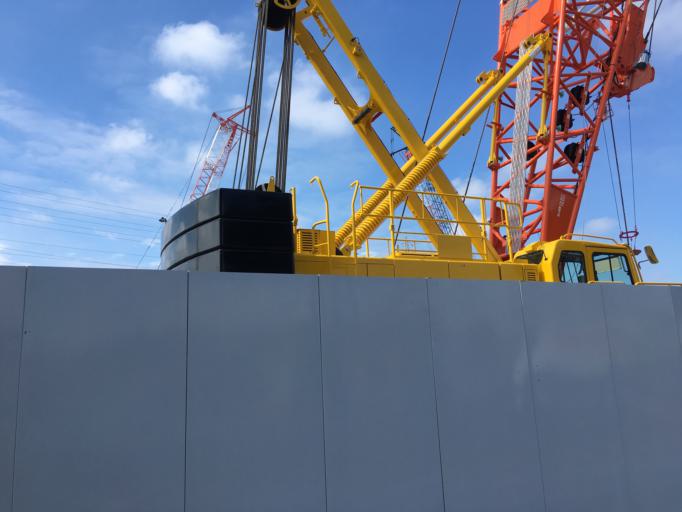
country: JP
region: Chiba
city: Matsudo
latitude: 35.8180
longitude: 139.9348
